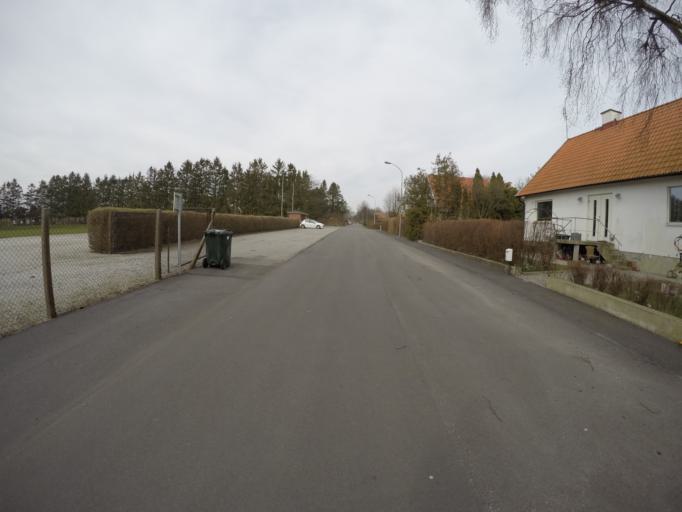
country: SE
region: Skane
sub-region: Ystads Kommun
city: Kopingebro
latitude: 55.4372
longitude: 14.1098
